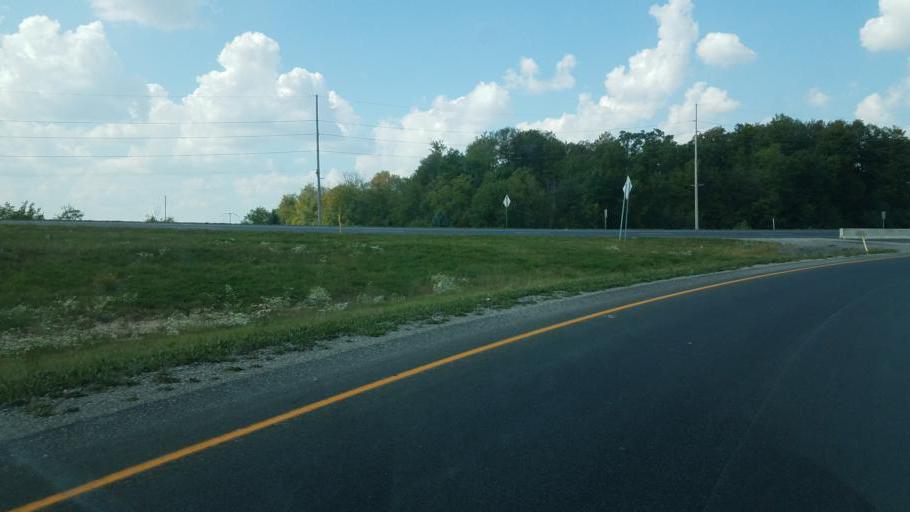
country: US
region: Indiana
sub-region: Allen County
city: Fort Wayne
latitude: 41.1660
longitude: -85.1078
